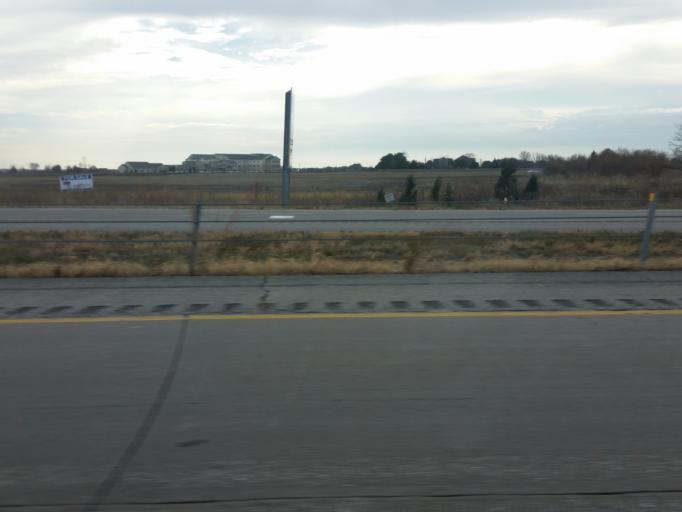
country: US
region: Iowa
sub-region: Scott County
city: Bettendorf
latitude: 41.5962
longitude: -90.5373
